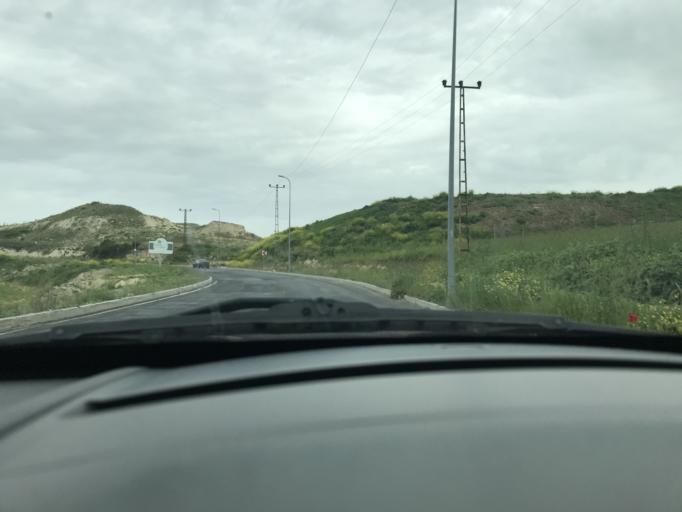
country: TR
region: Istanbul
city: Esenyurt
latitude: 41.0950
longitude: 28.6803
